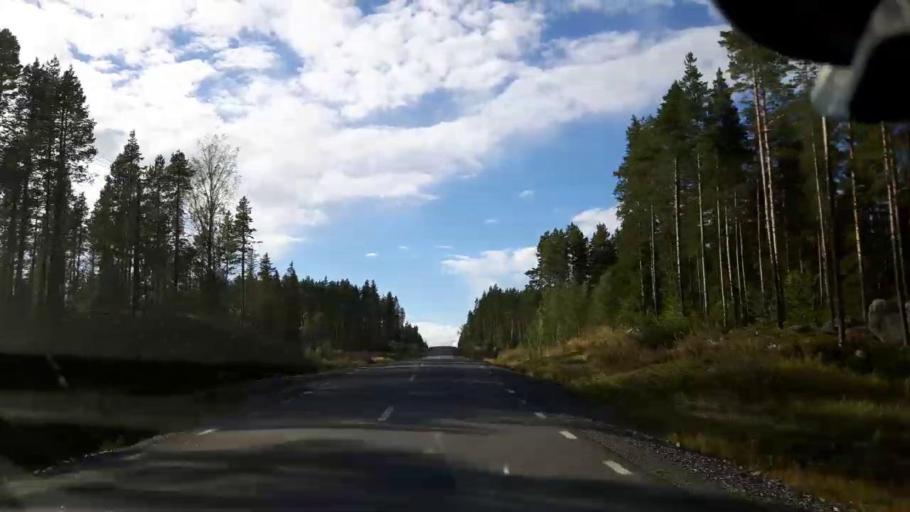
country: SE
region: Jaemtland
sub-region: Stroemsunds Kommun
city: Stroemsund
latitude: 63.5621
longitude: 15.8019
